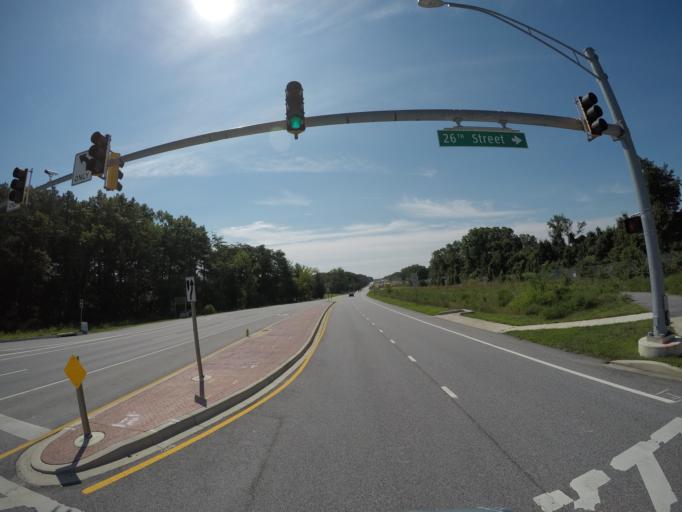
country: US
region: Maryland
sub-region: Anne Arundel County
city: Fort Meade
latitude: 39.1280
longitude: -76.7358
